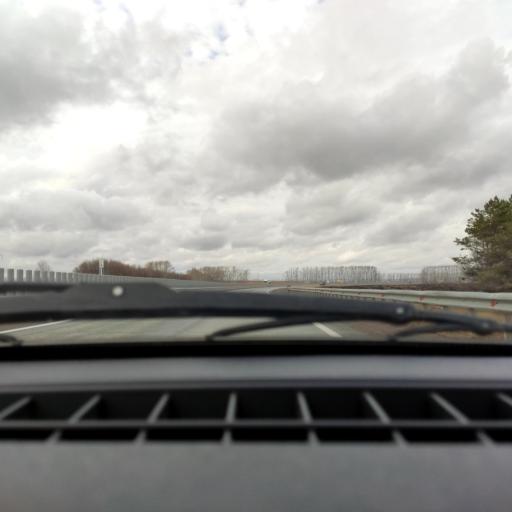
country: RU
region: Bashkortostan
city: Asanovo
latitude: 54.9202
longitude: 55.5828
